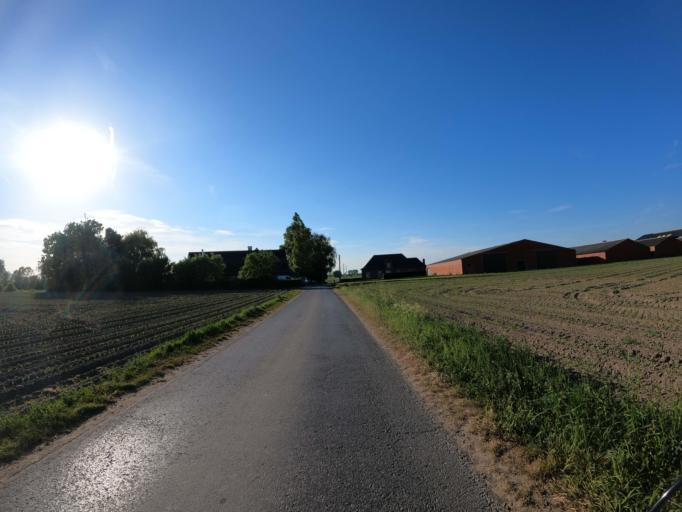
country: BE
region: Flanders
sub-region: Provincie West-Vlaanderen
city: Dentergem
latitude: 50.9918
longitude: 3.4574
